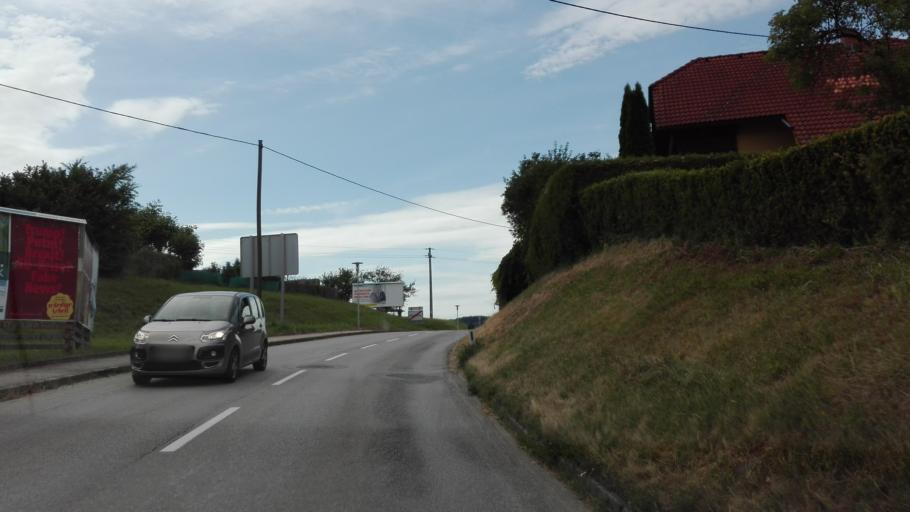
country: AT
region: Upper Austria
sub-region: Politischer Bezirk Grieskirchen
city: Grieskirchen
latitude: 48.2396
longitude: 13.8226
